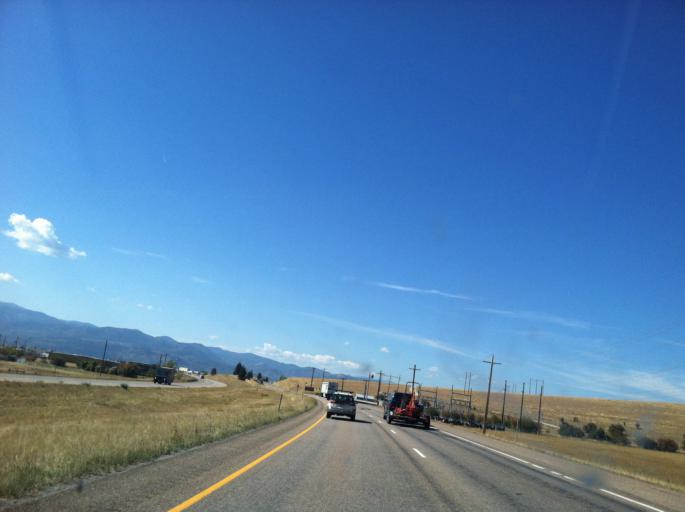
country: US
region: Montana
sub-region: Missoula County
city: Orchard Homes
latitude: 46.9373
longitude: -114.0967
